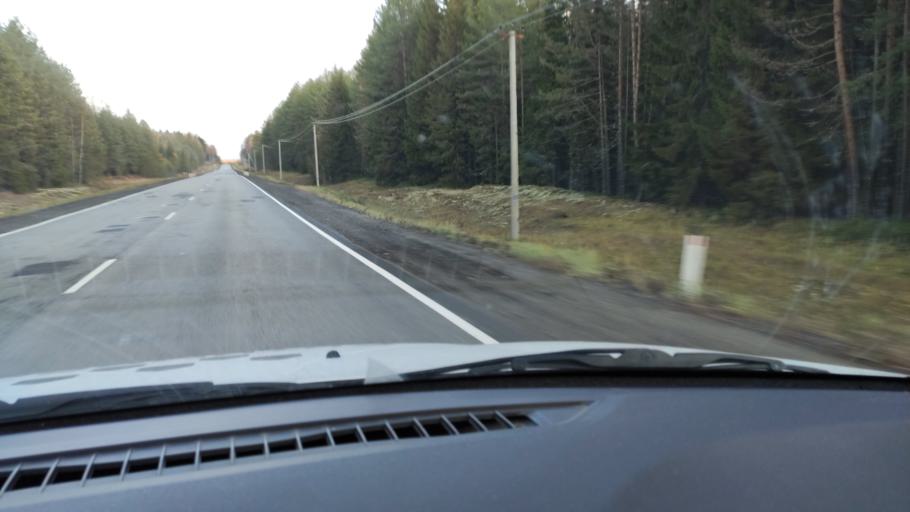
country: RU
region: Kirov
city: Belaya Kholunitsa
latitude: 58.9069
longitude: 51.0128
